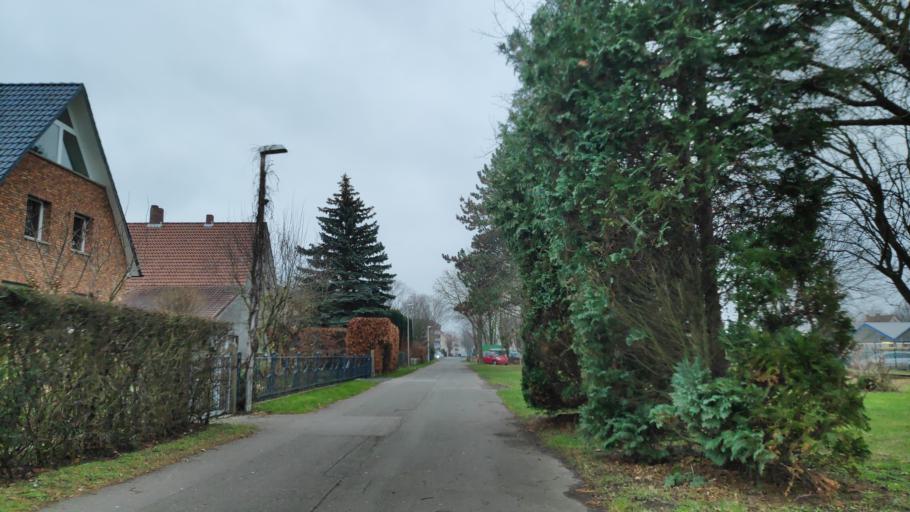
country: DE
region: North Rhine-Westphalia
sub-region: Regierungsbezirk Detmold
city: Minden
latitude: 52.2935
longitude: 8.8866
